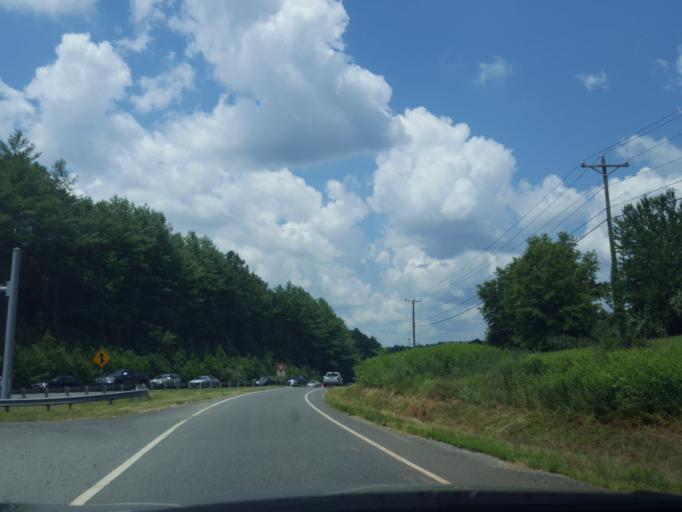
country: US
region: Virginia
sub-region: City of Charlottesville
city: Charlottesville
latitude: 38.0141
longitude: -78.3963
